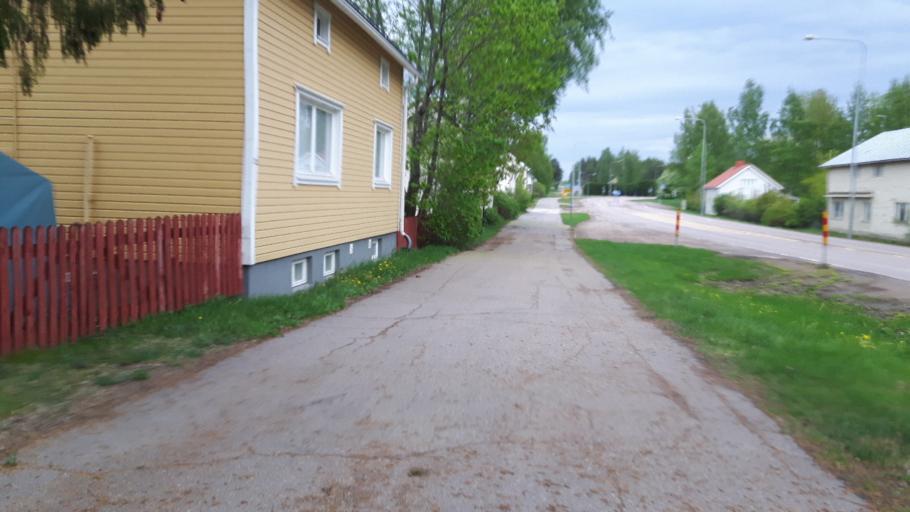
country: FI
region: Kymenlaakso
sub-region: Kotka-Hamina
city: Hamina
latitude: 60.5620
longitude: 27.2181
